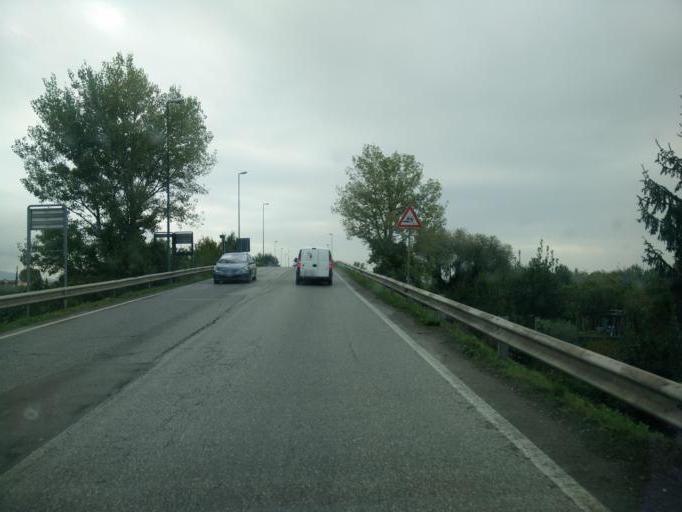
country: IT
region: Tuscany
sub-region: Province of Florence
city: Campi Bisenzio
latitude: 43.8329
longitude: 11.1328
